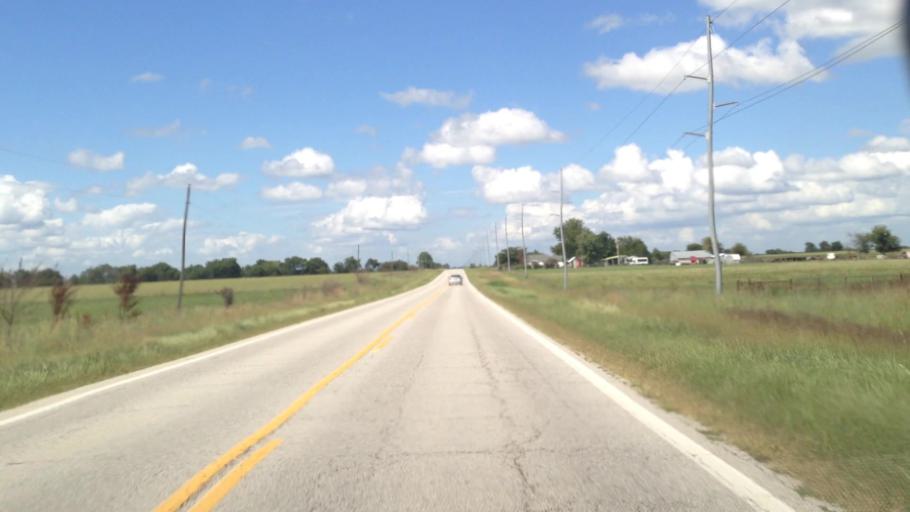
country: US
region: Kansas
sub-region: Labette County
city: Chetopa
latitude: 36.9502
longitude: -95.0834
